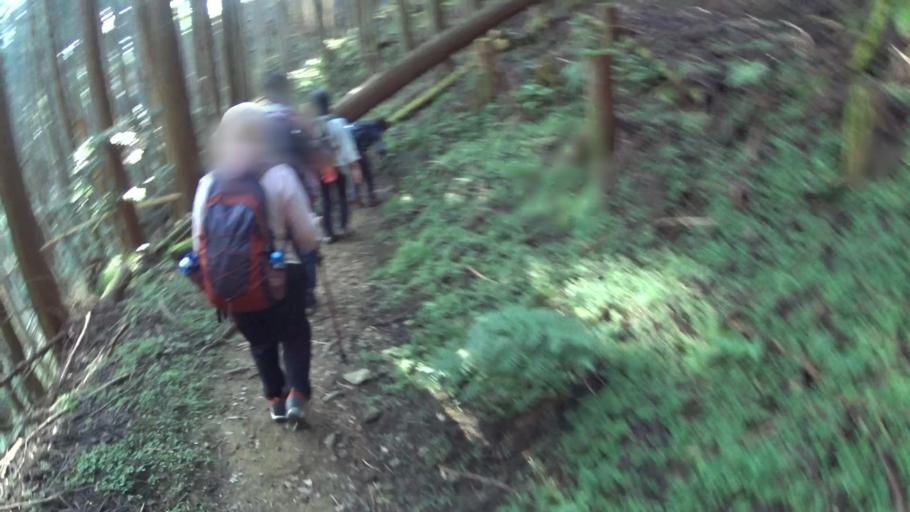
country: JP
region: Shiga Prefecture
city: Kitahama
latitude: 35.1085
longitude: 135.8425
